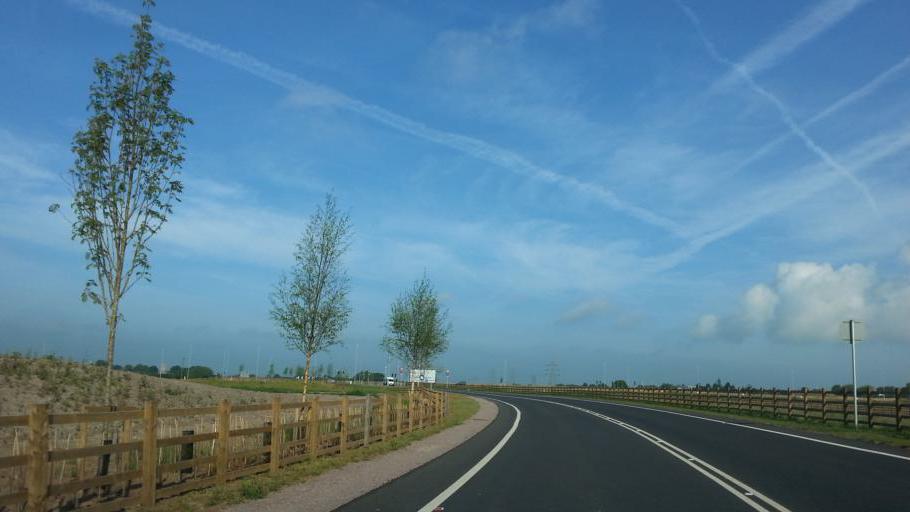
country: GB
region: England
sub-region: Nottinghamshire
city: Newark on Trent
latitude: 53.0523
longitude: -0.8026
